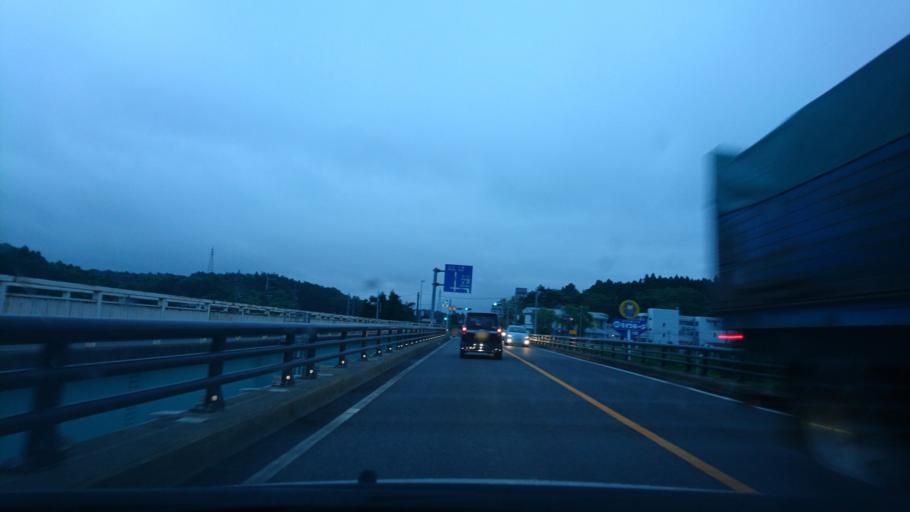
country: JP
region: Iwate
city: Ichinoseki
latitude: 38.7983
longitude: 141.0549
